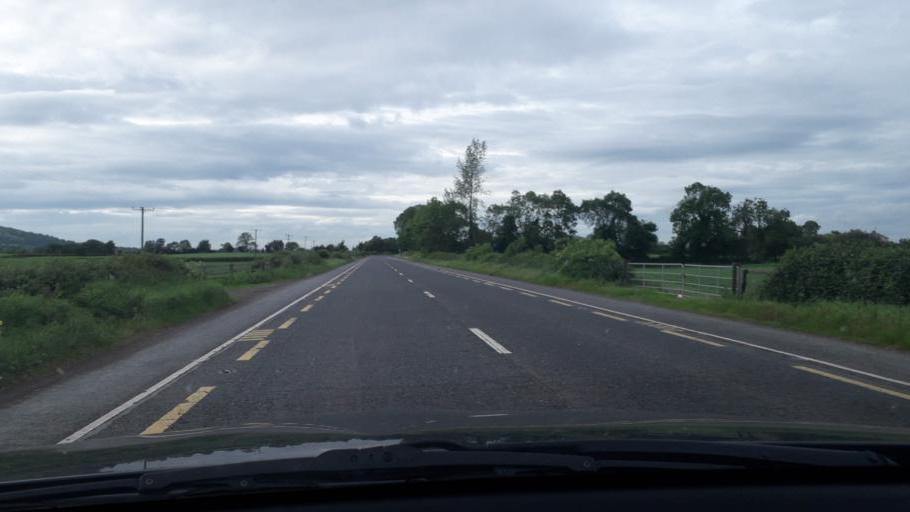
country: IE
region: Leinster
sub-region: County Carlow
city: Carlow
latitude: 52.8008
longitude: -6.9508
